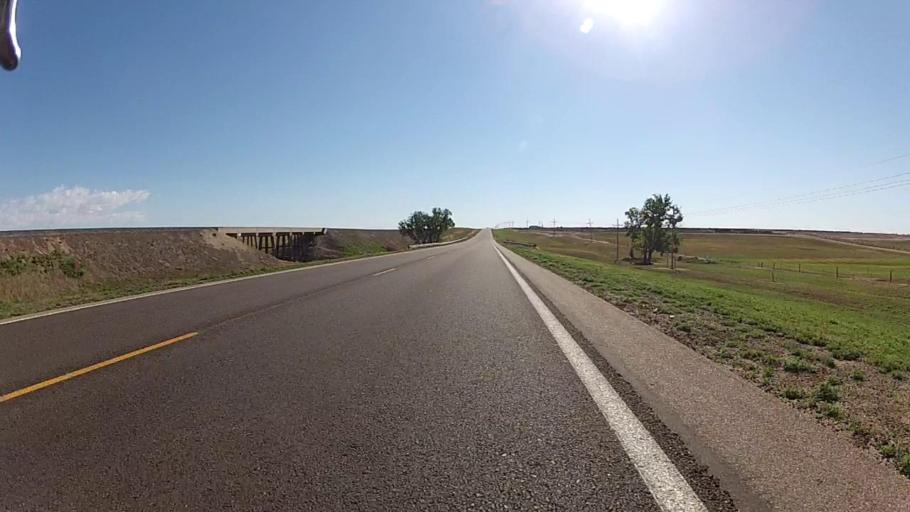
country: US
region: Kansas
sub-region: Haskell County
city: Sublette
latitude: 37.5651
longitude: -100.5554
